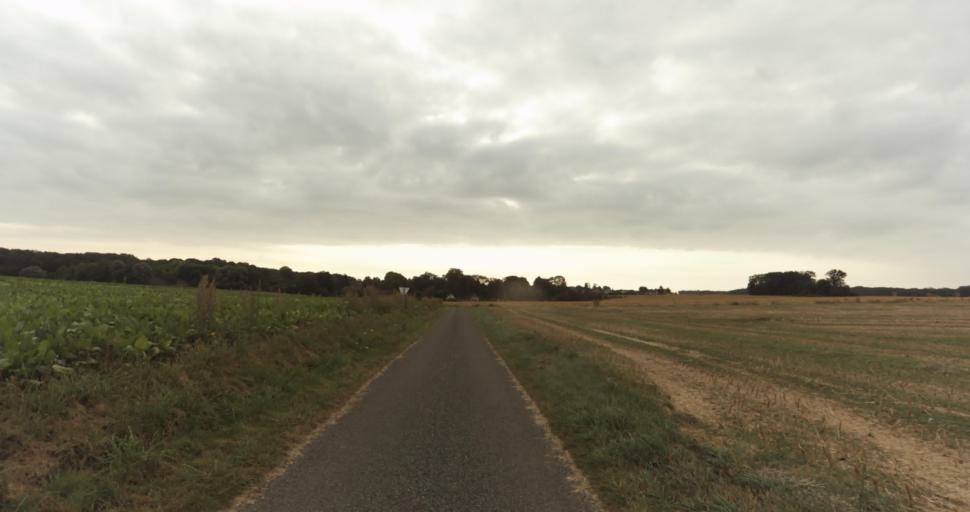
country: FR
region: Haute-Normandie
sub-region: Departement de l'Eure
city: Saint-Germain-sur-Avre
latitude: 48.8084
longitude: 1.2766
